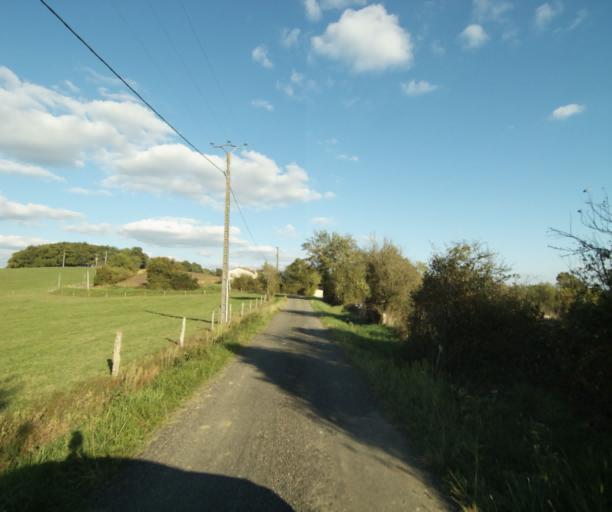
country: FR
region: Midi-Pyrenees
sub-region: Departement du Gers
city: Eauze
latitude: 43.7617
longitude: 0.1113
